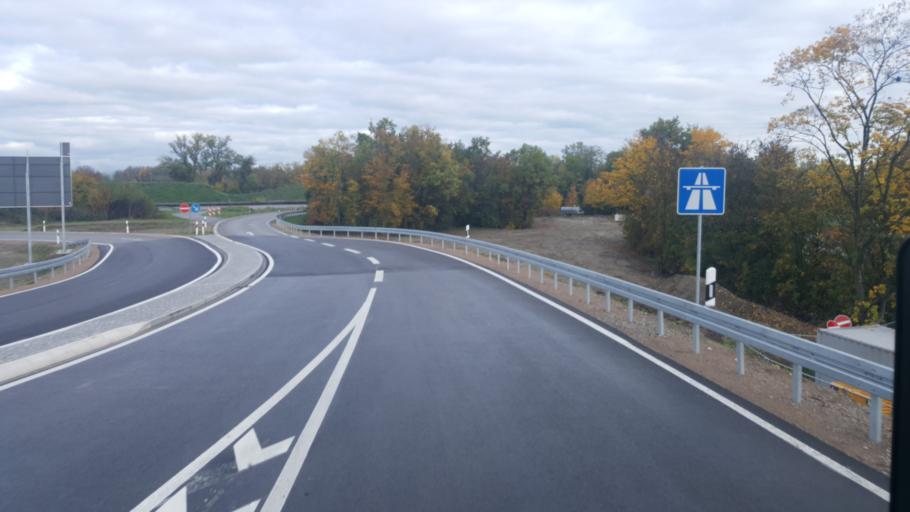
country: DE
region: Baden-Wuerttemberg
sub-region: Freiburg Region
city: Neuenburg am Rhein
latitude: 47.8144
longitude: 7.5552
